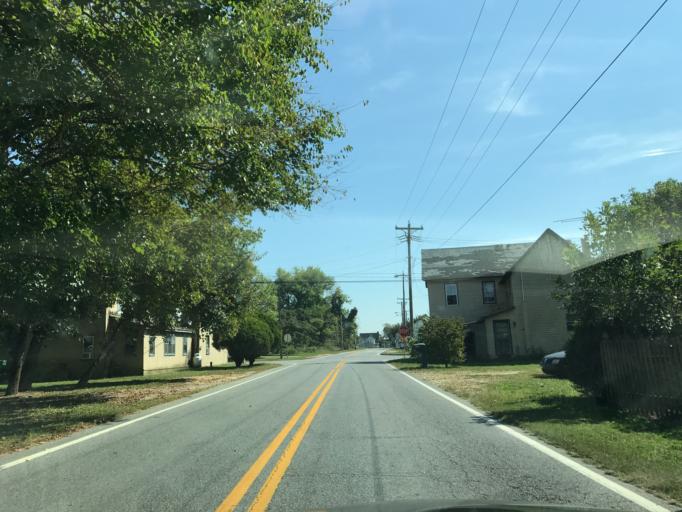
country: US
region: Delaware
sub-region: New Castle County
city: Townsend
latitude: 39.3096
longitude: -75.8263
